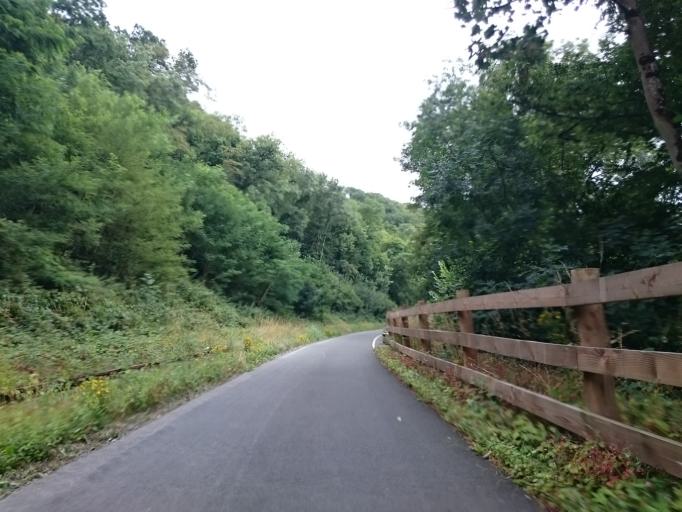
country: FR
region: Lower Normandy
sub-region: Departement du Calvados
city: Thury-Harcourt
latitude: 49.0044
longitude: -0.4650
